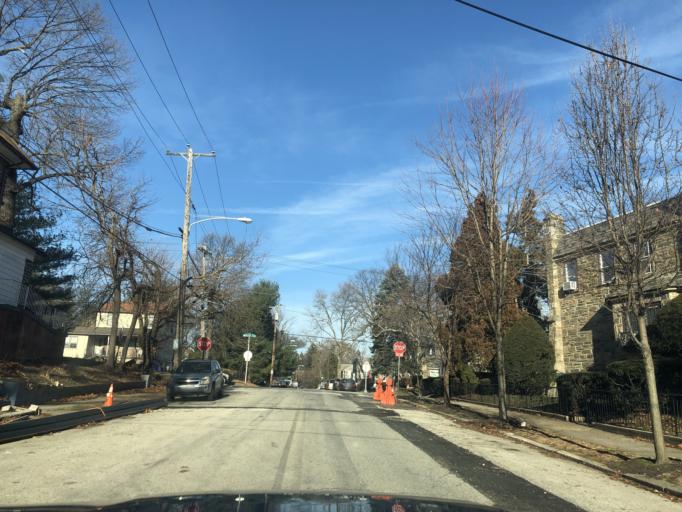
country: US
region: Pennsylvania
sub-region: Montgomery County
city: Bala-Cynwyd
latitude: 39.9890
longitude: -75.2396
